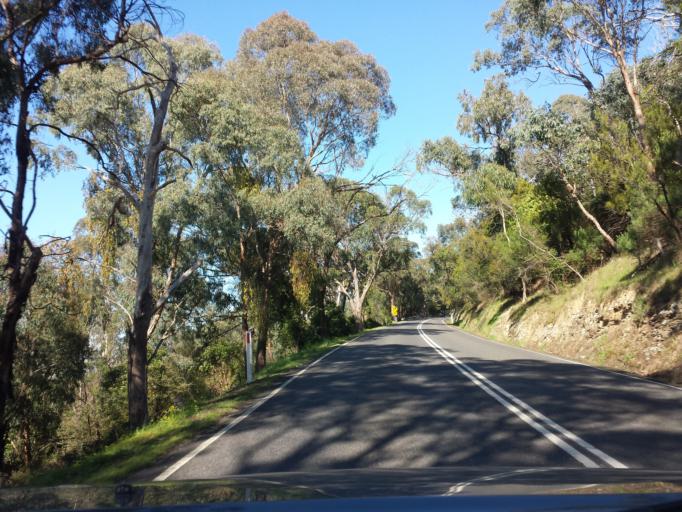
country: AU
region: Victoria
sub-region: Yarra Ranges
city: Yarra Glen
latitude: -37.6490
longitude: 145.3584
